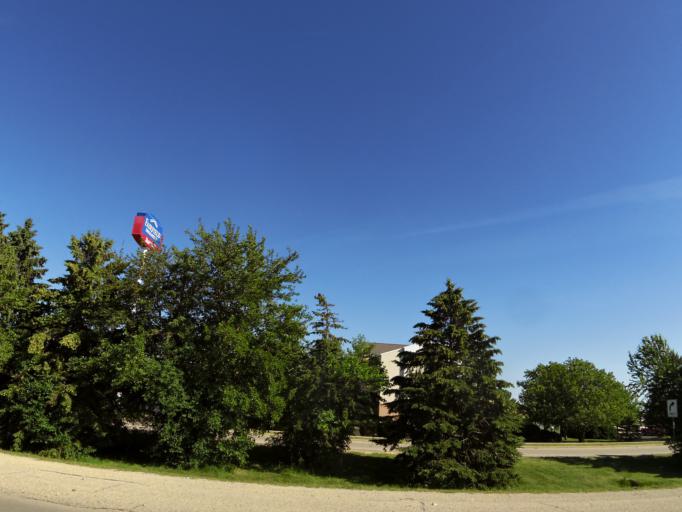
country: US
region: Wisconsin
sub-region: Rock County
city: Beloit
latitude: 42.5239
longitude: -88.9843
